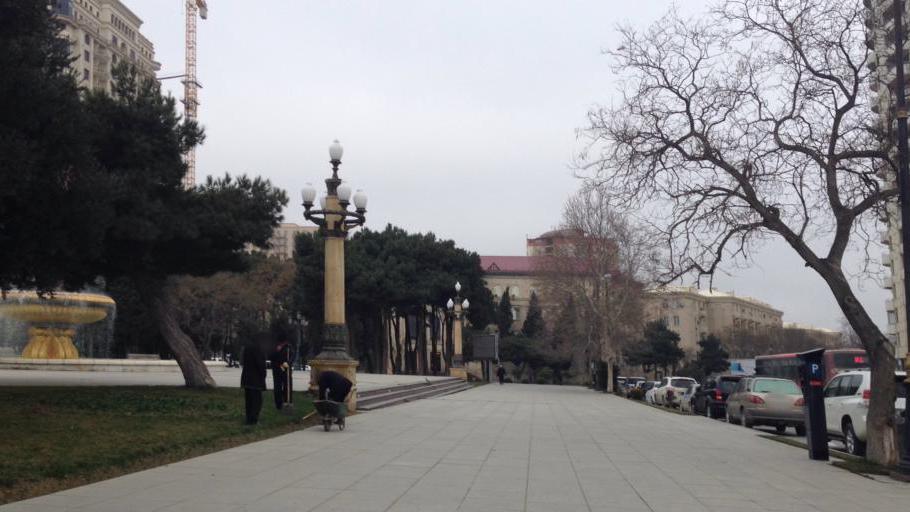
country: AZ
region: Baki
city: Badamdar
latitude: 40.3732
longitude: 49.8185
